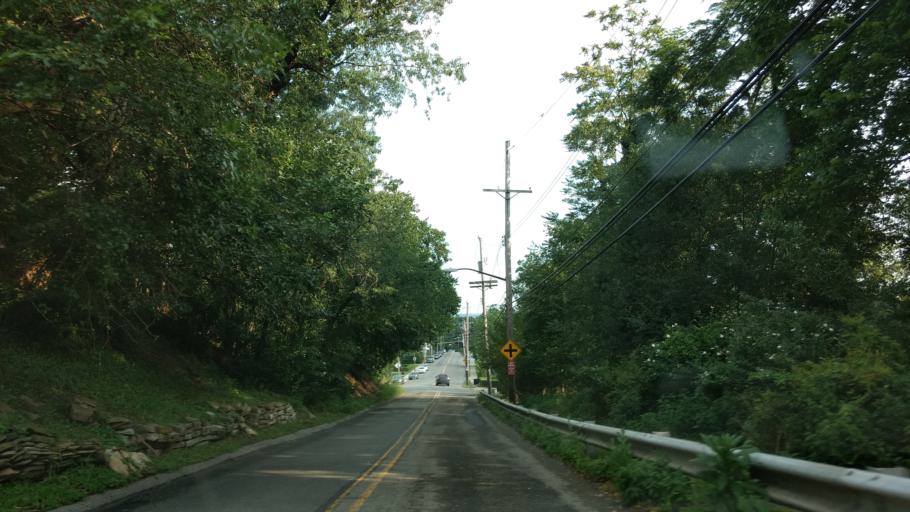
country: US
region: Pennsylvania
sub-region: Allegheny County
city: Bellevue
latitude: 40.4897
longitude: -80.0349
